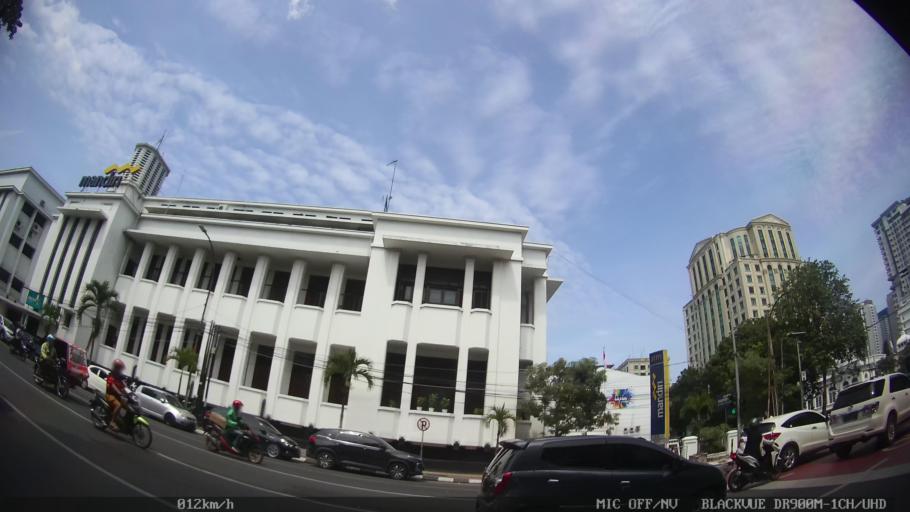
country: ID
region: North Sumatra
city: Medan
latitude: 3.5894
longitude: 98.6781
